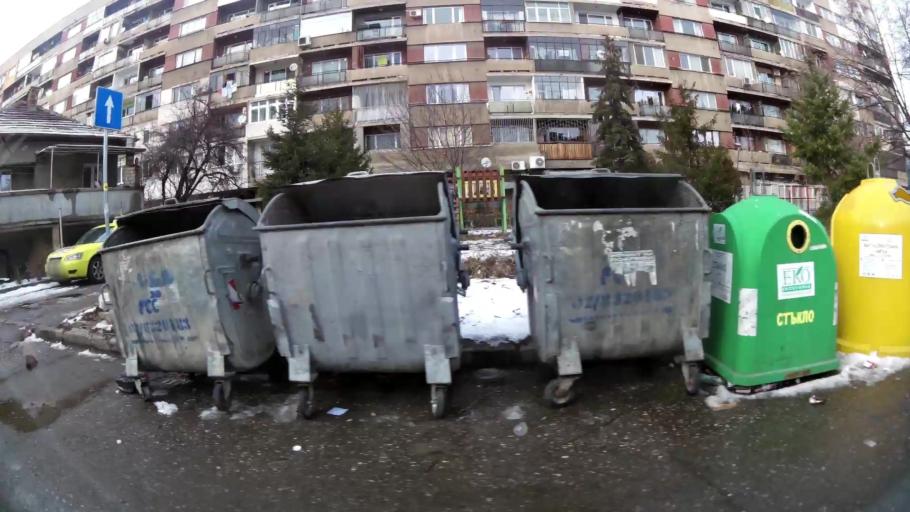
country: BG
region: Sofia-Capital
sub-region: Stolichna Obshtina
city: Sofia
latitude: 42.6988
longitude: 23.3671
